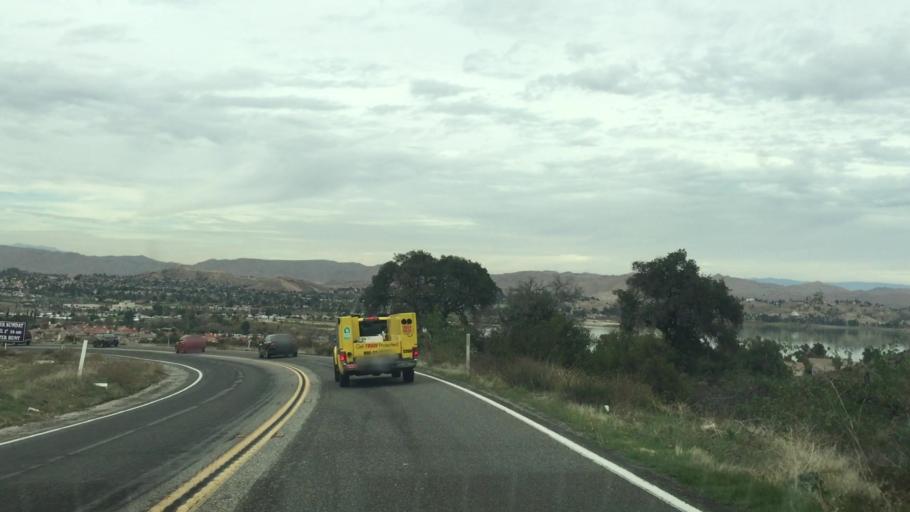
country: US
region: California
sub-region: Riverside County
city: Lakeland Village
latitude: 33.6497
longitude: -117.3774
